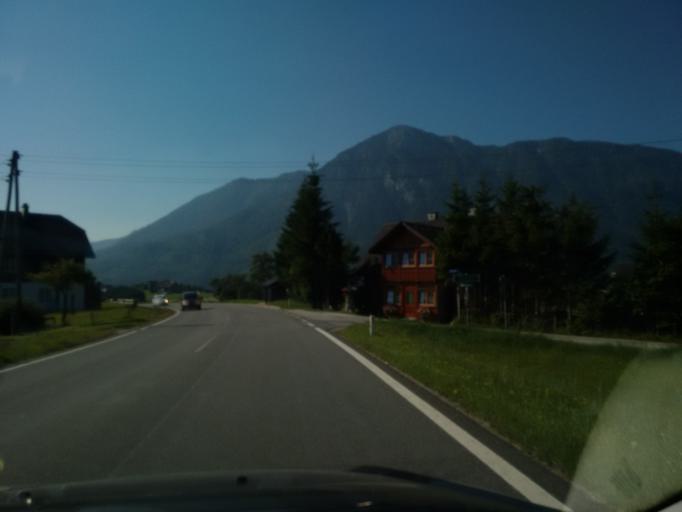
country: AT
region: Styria
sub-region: Politischer Bezirk Liezen
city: Bad Aussee
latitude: 47.6140
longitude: 13.7641
